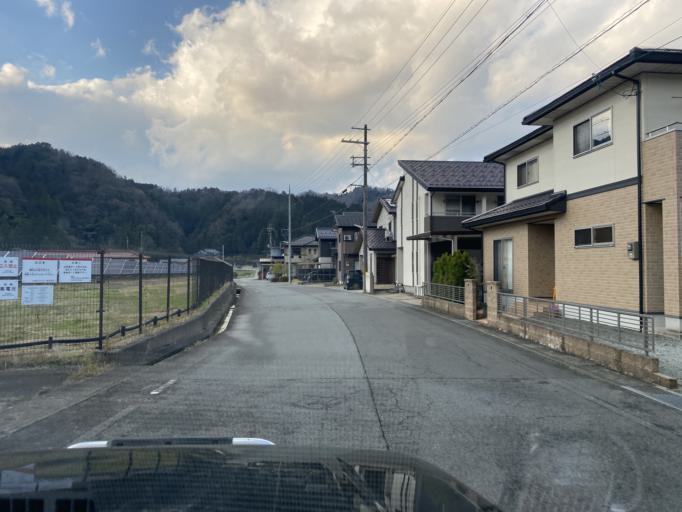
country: JP
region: Hyogo
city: Toyooka
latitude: 35.4651
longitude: 134.7590
